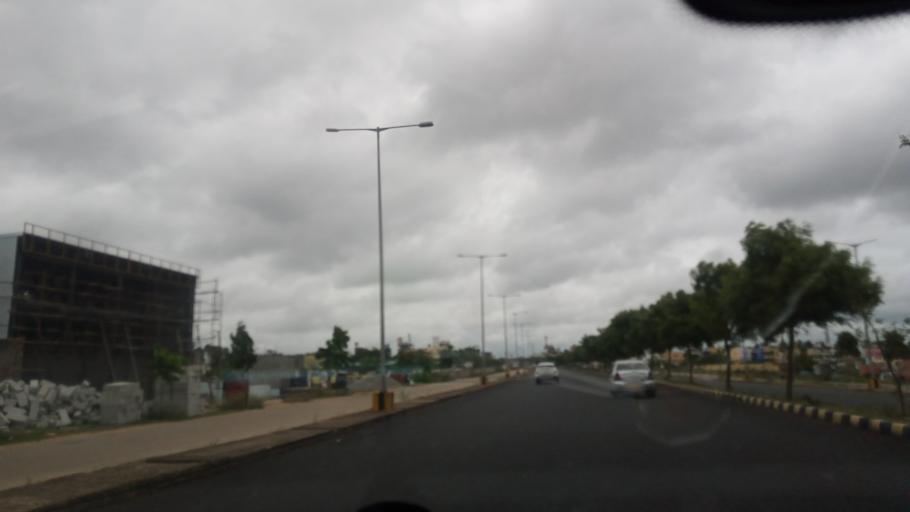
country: IN
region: Karnataka
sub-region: Mysore
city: Mysore
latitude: 12.3261
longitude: 76.5967
